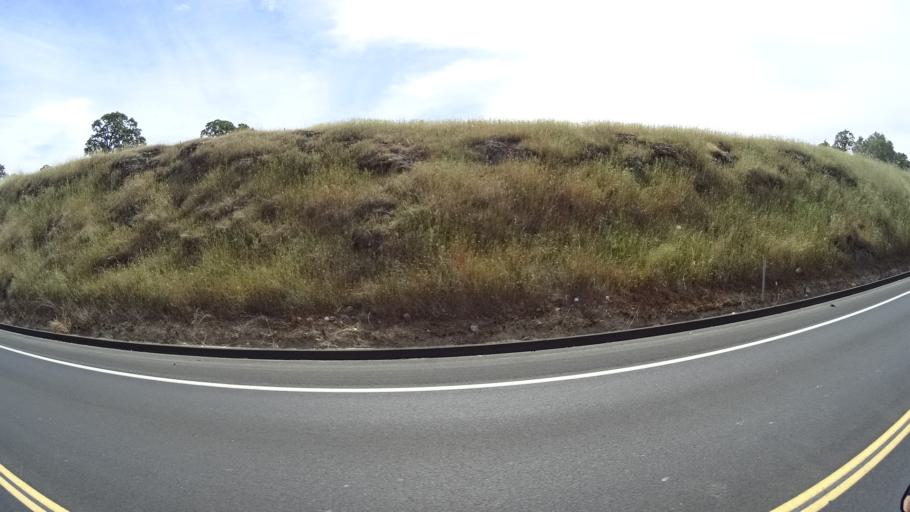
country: US
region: California
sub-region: Placer County
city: Loomis
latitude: 38.8572
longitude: -121.2172
